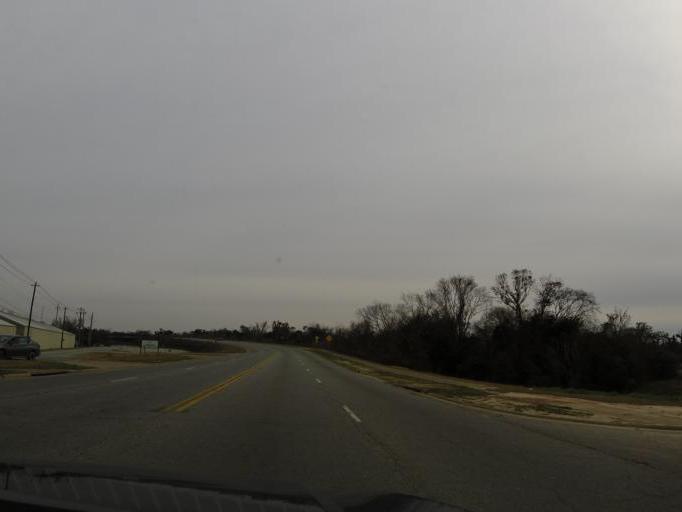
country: US
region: Georgia
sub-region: Decatur County
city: Bainbridge
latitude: 30.9125
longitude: -84.5846
